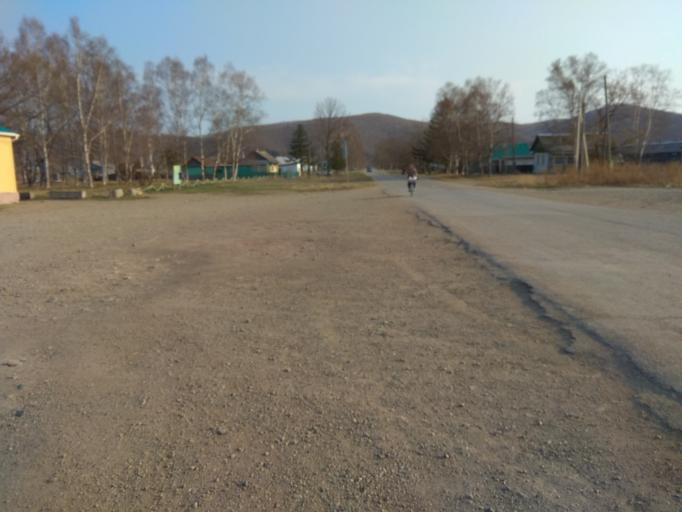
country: RU
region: Primorskiy
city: Lazo
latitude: 43.3076
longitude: 134.6041
